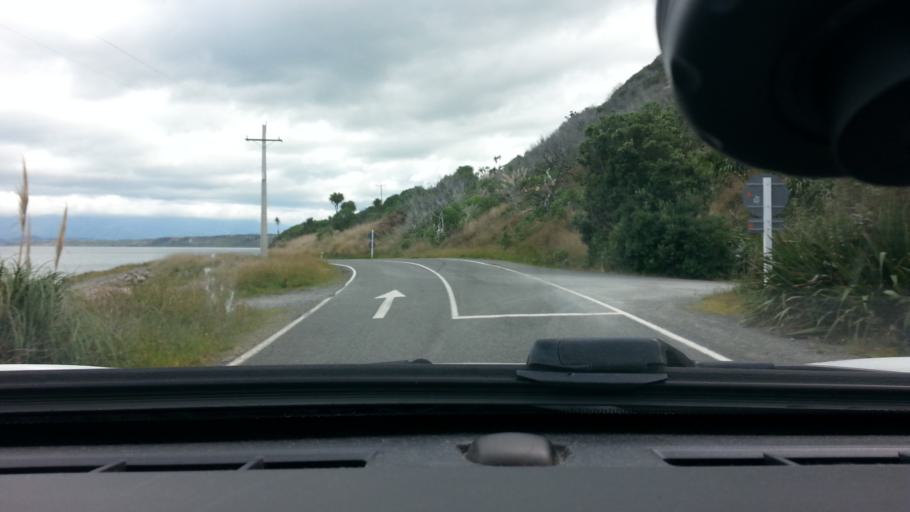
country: NZ
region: Wellington
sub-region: South Wairarapa District
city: Waipawa
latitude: -41.4500
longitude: 175.2217
